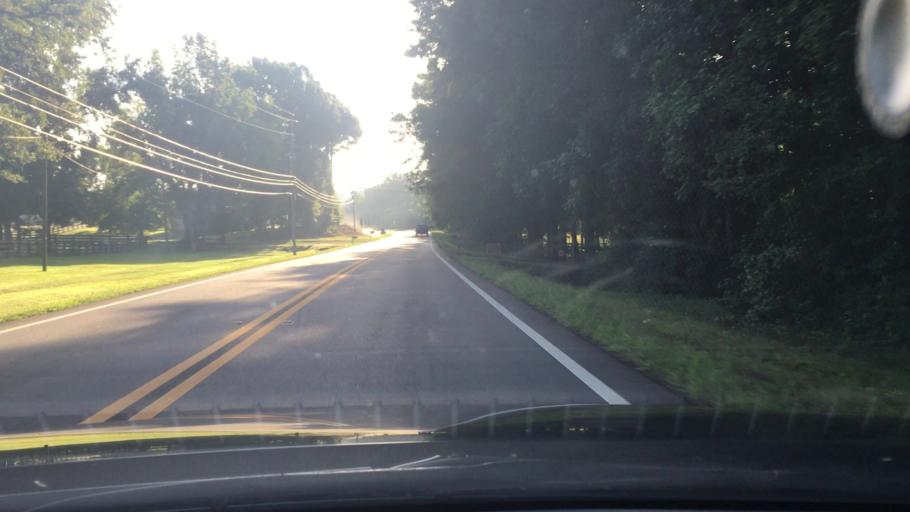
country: US
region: Georgia
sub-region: Fayette County
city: Peachtree City
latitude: 33.3929
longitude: -84.6340
